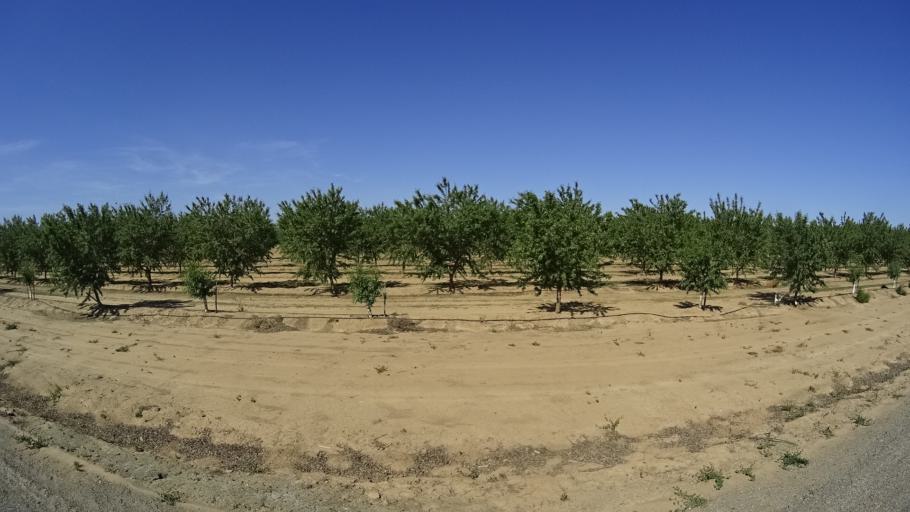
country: US
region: California
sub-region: Glenn County
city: Willows
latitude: 39.6254
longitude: -122.1788
